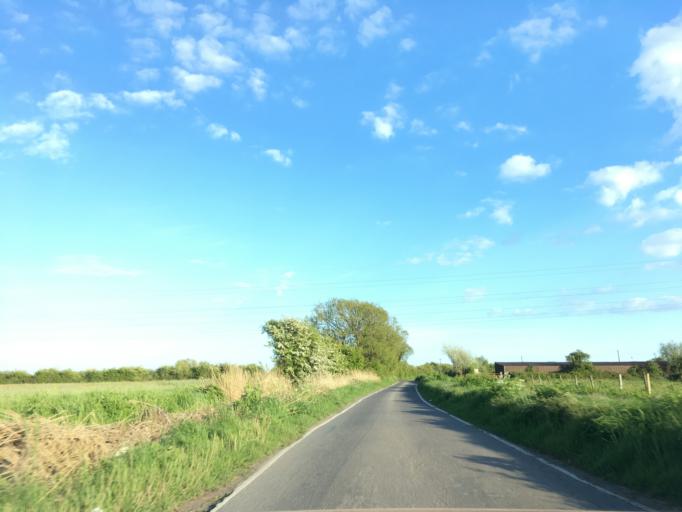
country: GB
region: Wales
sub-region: Newport
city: Marshfield
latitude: 51.5202
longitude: -3.0686
